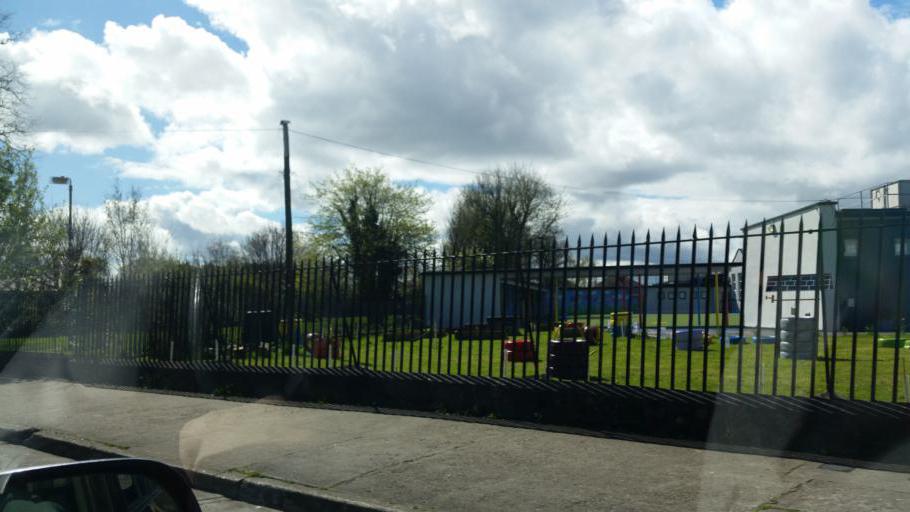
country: IE
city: Killester
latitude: 53.3787
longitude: -6.2048
